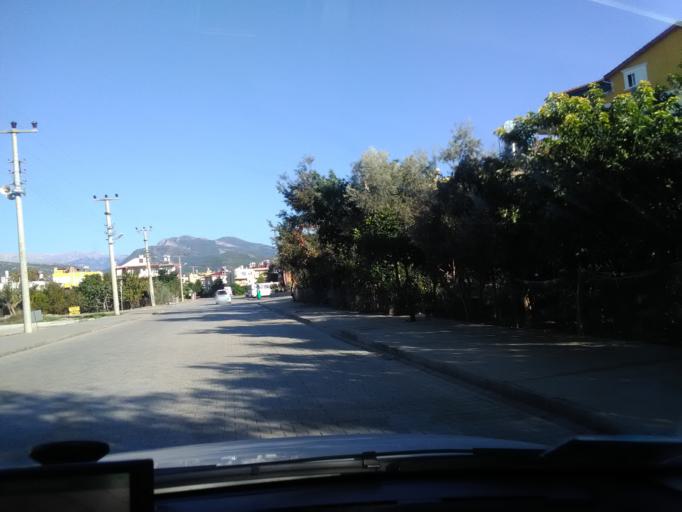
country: TR
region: Antalya
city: Gazipasa
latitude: 36.2662
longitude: 32.3217
